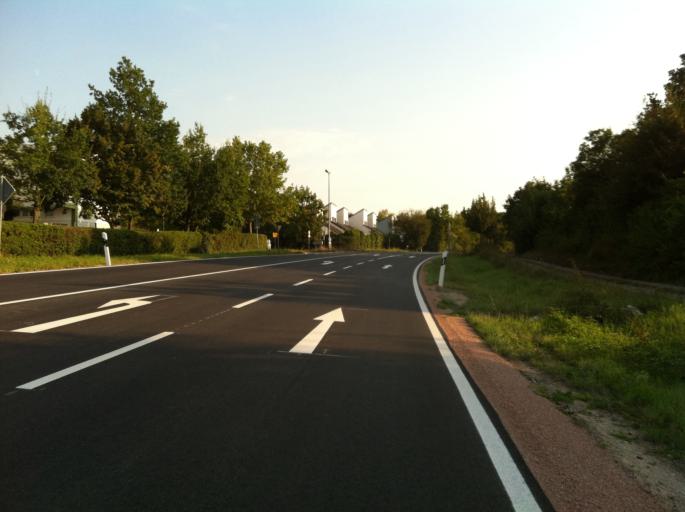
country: DE
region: Rheinland-Pfalz
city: Ober-Olm
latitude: 49.9673
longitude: 8.1867
